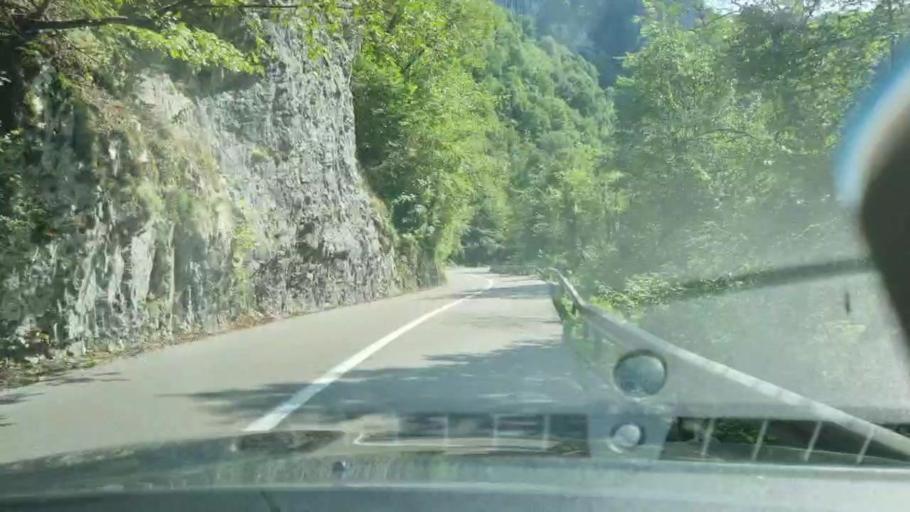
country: BA
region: Federation of Bosnia and Herzegovina
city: Bosanska Krupa
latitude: 44.8676
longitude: 16.0962
